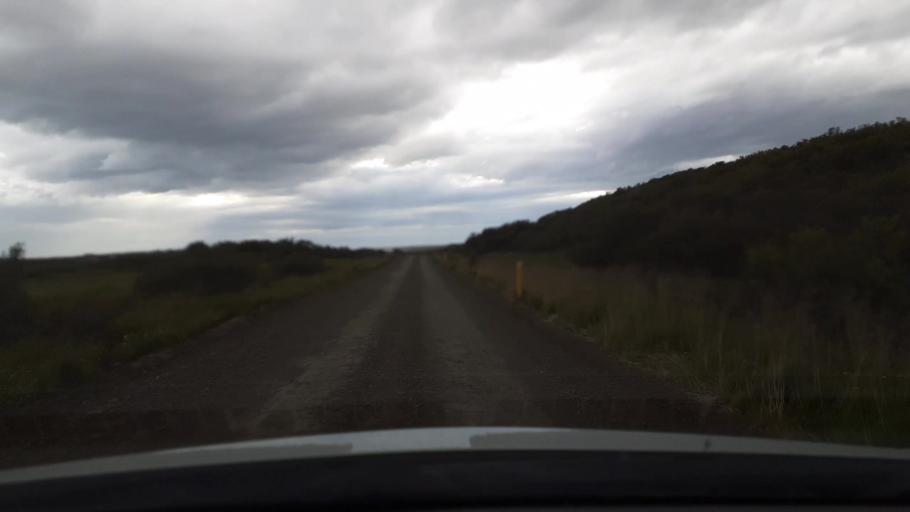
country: IS
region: West
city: Borgarnes
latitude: 64.6033
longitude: -21.9694
